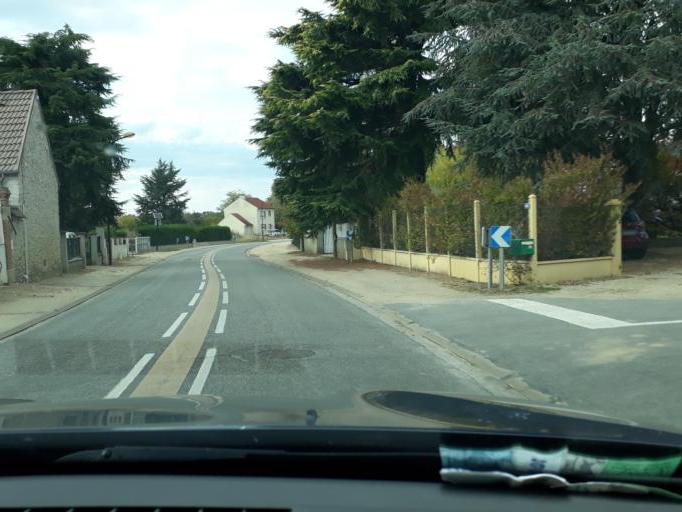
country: FR
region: Centre
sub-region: Departement du Loiret
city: Saint-Benoit-sur-Loire
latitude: 47.8138
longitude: 2.3019
